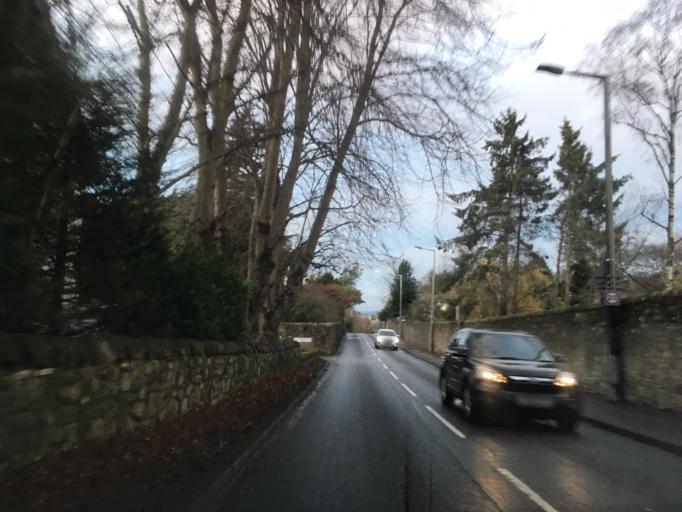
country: GB
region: Scotland
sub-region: Edinburgh
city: Colinton
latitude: 55.9510
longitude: -3.2557
